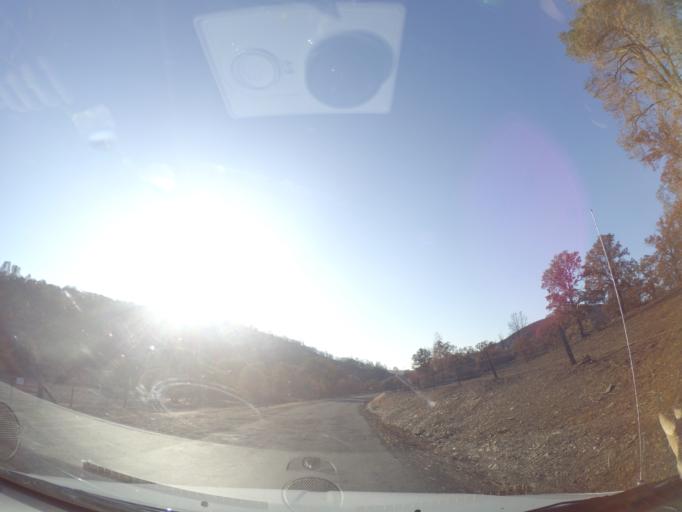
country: US
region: California
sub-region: Mariposa County
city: Mariposa
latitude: 37.5031
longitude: -120.0764
